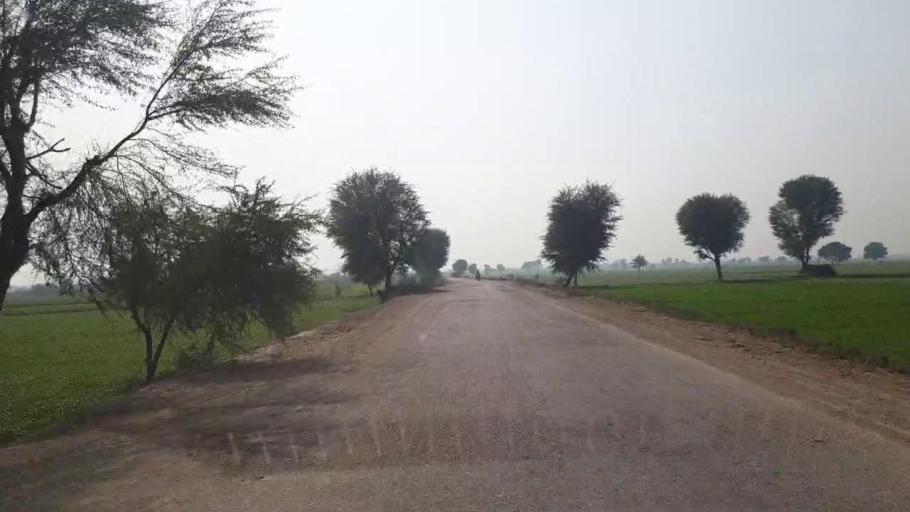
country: PK
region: Sindh
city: Hala
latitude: 25.8750
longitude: 68.4329
